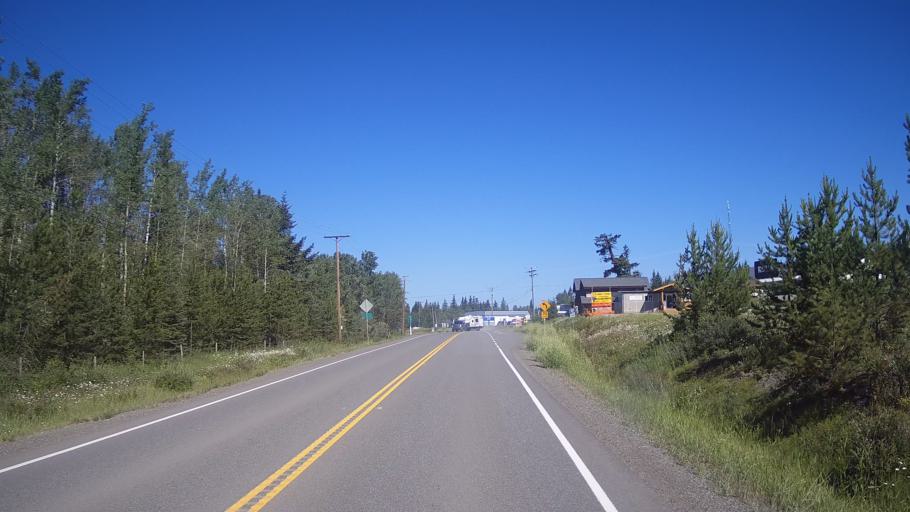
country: CA
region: British Columbia
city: Cache Creek
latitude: 51.5445
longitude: -120.9125
